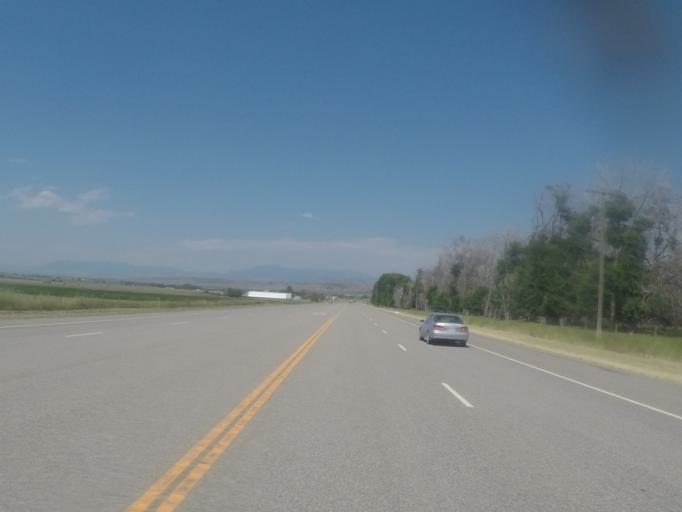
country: US
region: Montana
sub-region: Broadwater County
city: Townsend
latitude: 46.1535
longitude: -111.4647
